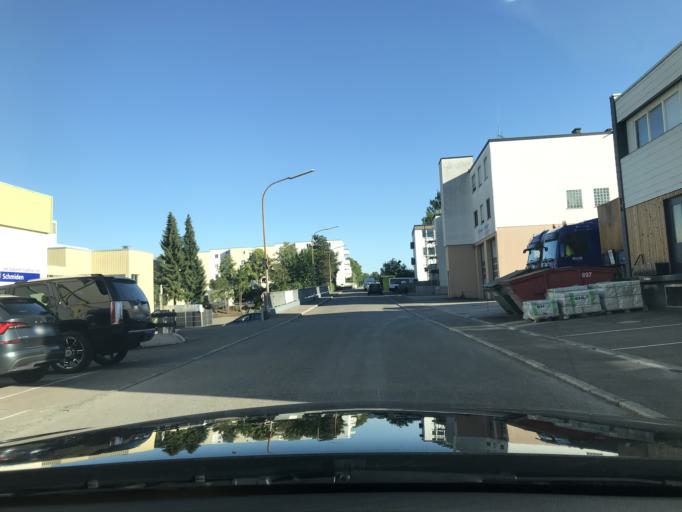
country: DE
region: Baden-Wuerttemberg
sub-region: Regierungsbezirk Stuttgart
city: Fellbach
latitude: 48.8294
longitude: 9.2597
